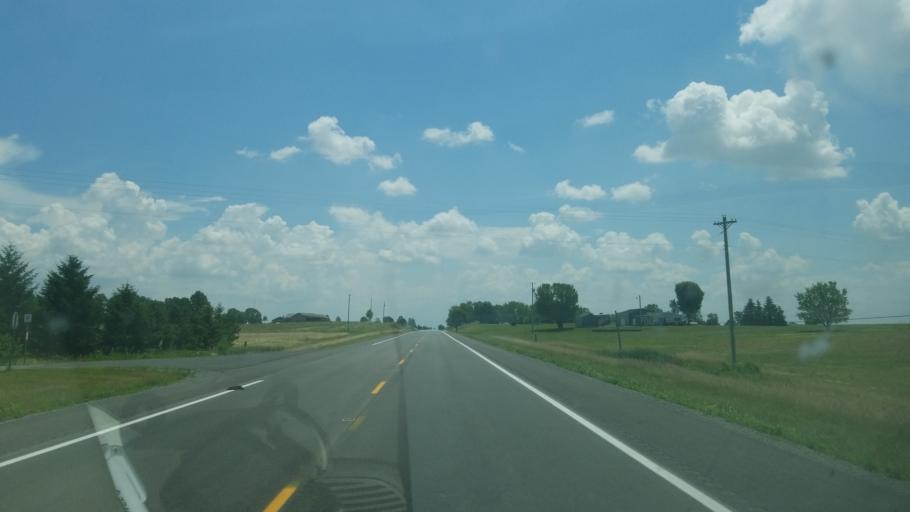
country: US
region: Ohio
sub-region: Hardin County
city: Ada
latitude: 40.7070
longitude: -83.7404
